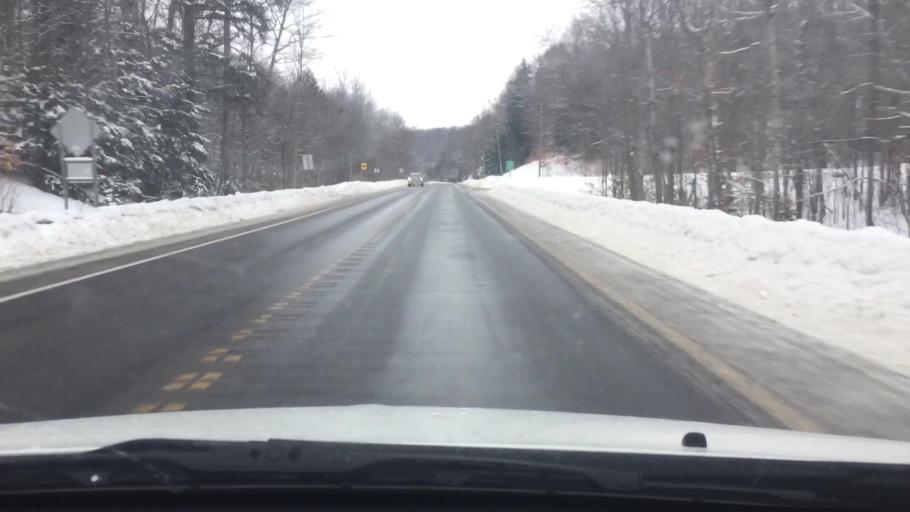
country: US
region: Michigan
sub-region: Charlevoix County
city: East Jordan
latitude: 45.1174
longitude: -85.0611
